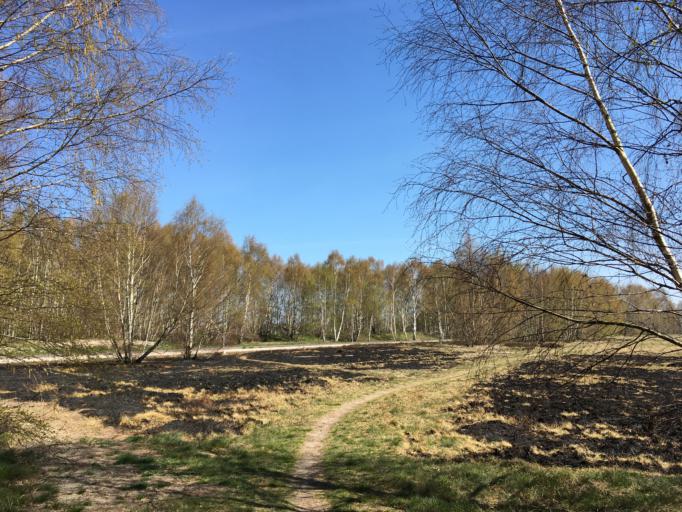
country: SE
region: Skane
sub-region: Bastads Kommun
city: Bastad
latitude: 56.4474
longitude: 12.9184
